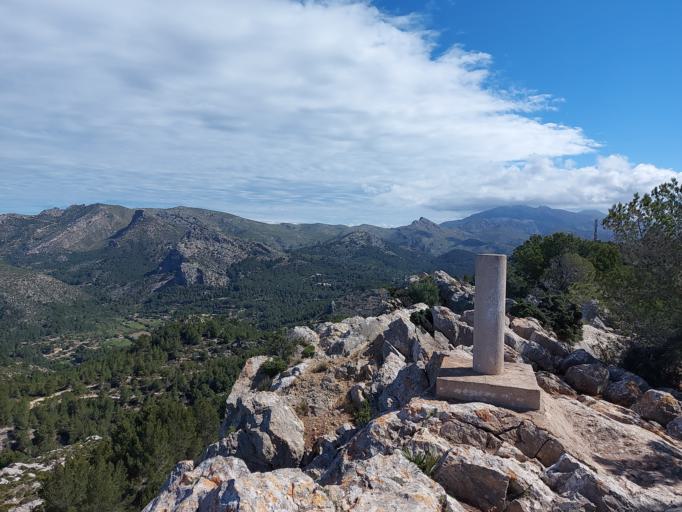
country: ES
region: Balearic Islands
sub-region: Illes Balears
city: Andratx
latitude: 39.5685
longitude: 2.3654
